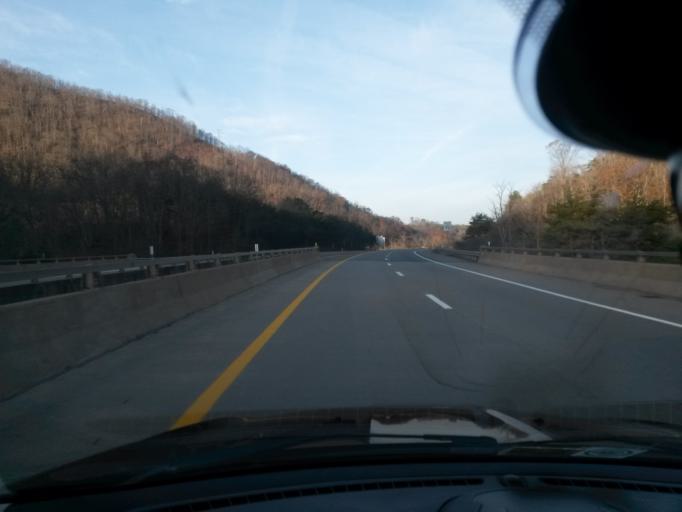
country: US
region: West Virginia
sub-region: Greenbrier County
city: White Sulphur Springs
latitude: 37.7706
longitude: -80.3685
